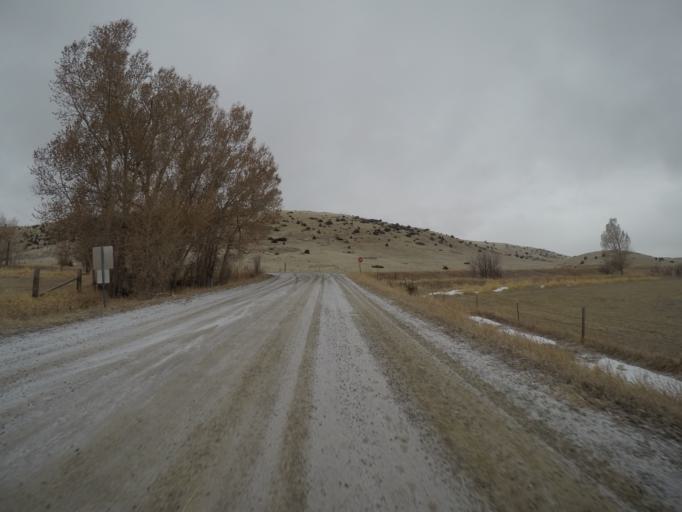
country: US
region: Montana
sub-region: Stillwater County
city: Absarokee
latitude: 45.5225
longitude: -109.4696
